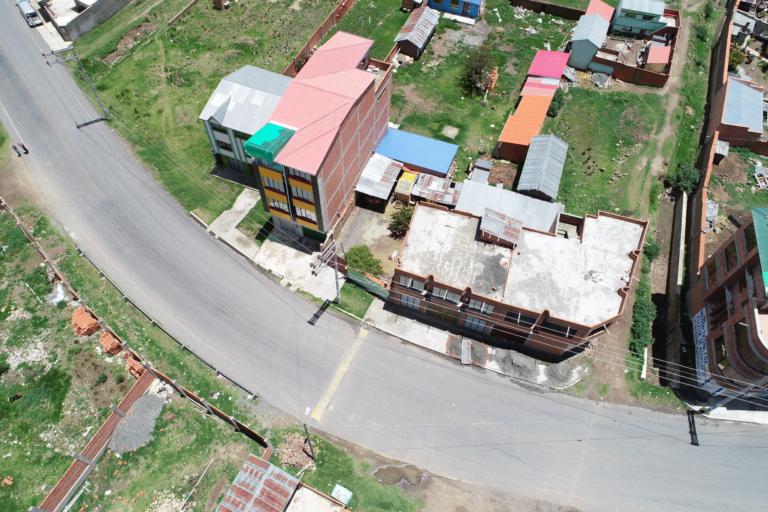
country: BO
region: La Paz
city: Achacachi
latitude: -16.0221
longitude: -68.7915
